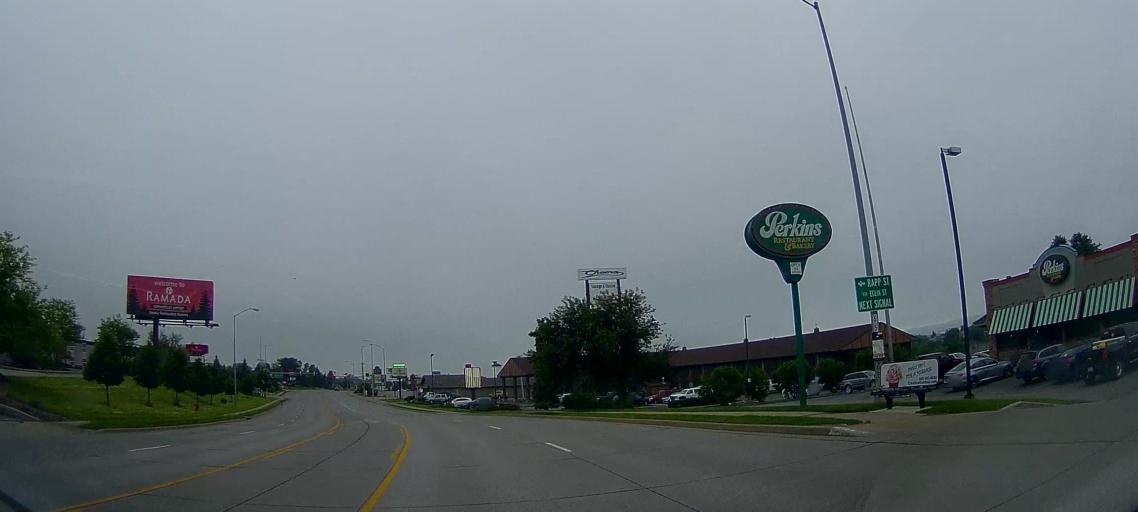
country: US
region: South Dakota
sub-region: Pennington County
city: Rapid City
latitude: 44.1021
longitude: -103.2035
